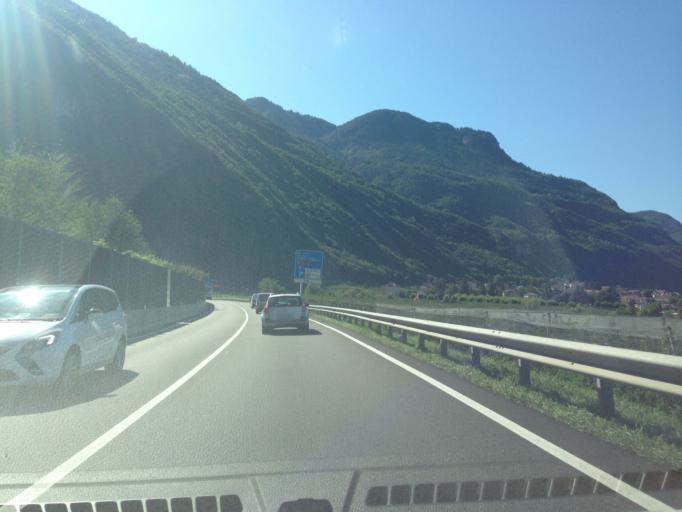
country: IT
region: Trentino-Alto Adige
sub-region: Bolzano
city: Pineta
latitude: 46.4373
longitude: 11.3445
